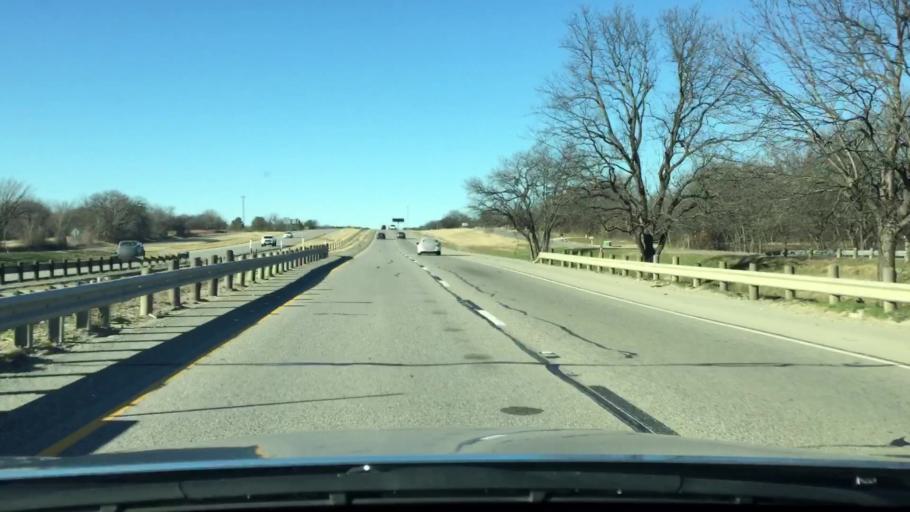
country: US
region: Texas
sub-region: Johnson County
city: Alvarado
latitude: 32.3619
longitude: -97.1994
